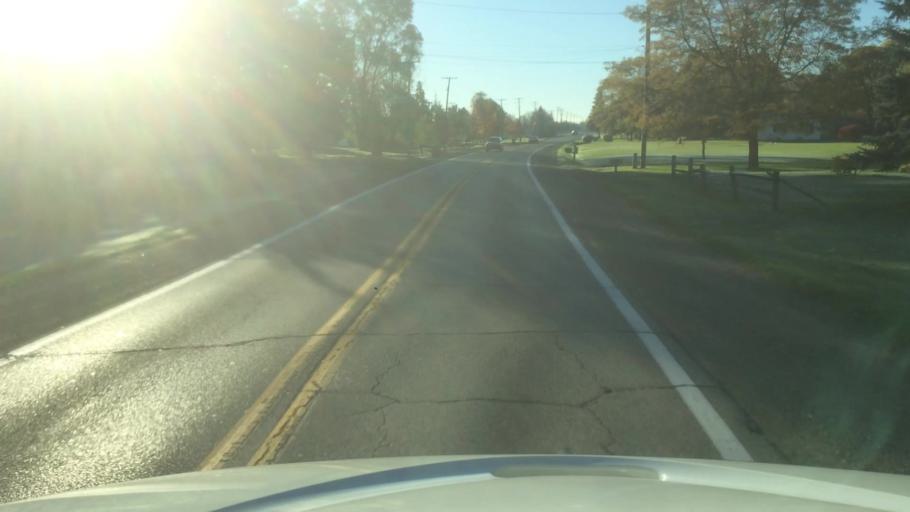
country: US
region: Michigan
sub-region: Macomb County
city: Shelby
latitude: 42.6789
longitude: -82.9451
